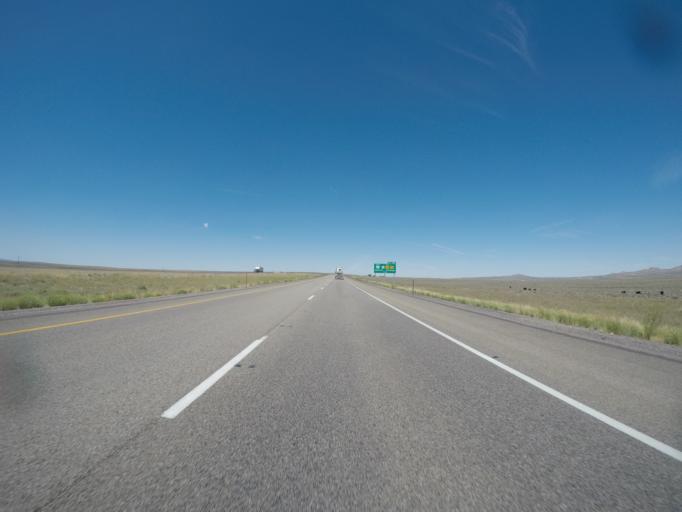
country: US
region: Wyoming
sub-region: Carbon County
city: Saratoga
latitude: 41.7423
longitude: -106.8001
